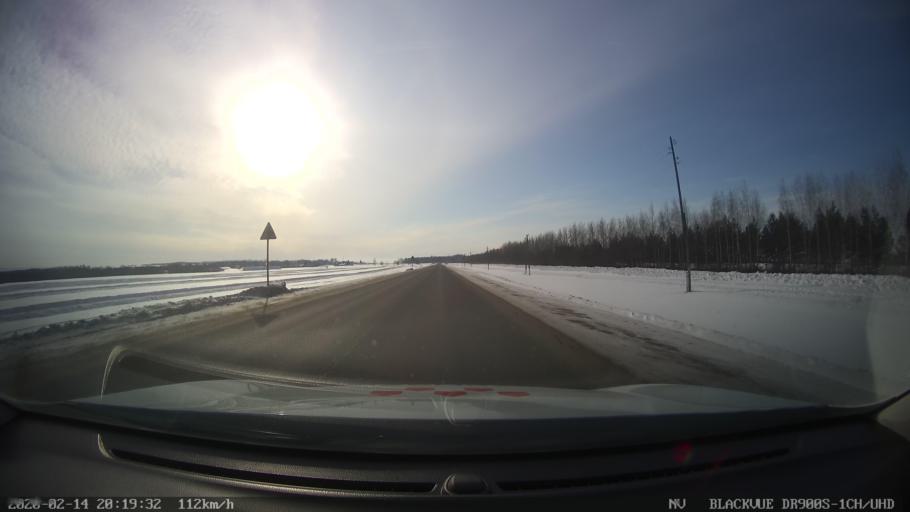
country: RU
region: Tatarstan
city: Verkhniy Uslon
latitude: 55.5699
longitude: 48.9012
